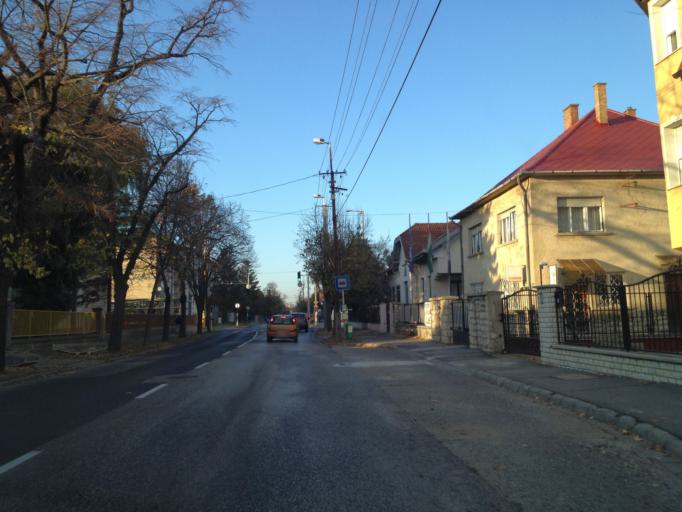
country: HU
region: Gyor-Moson-Sopron
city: Gyor
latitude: 47.6712
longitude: 17.6423
